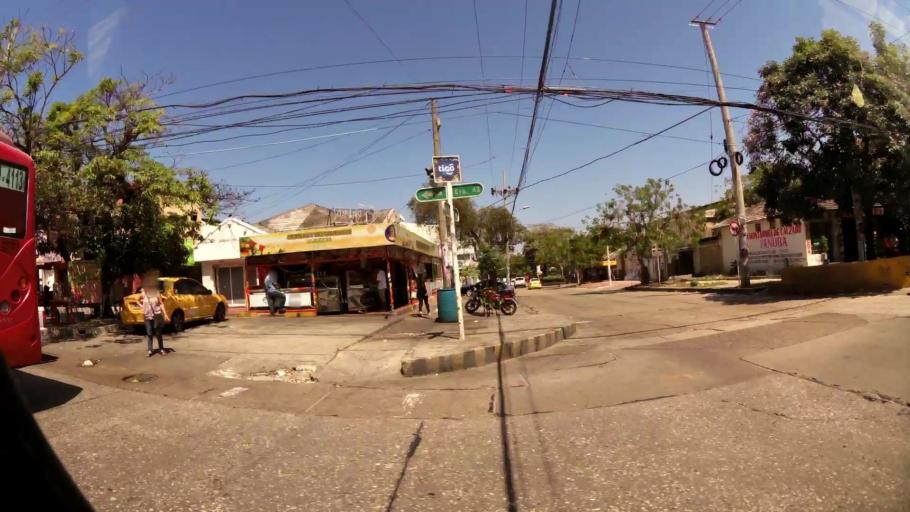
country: CO
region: Atlantico
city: Barranquilla
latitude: 10.9953
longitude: -74.8137
